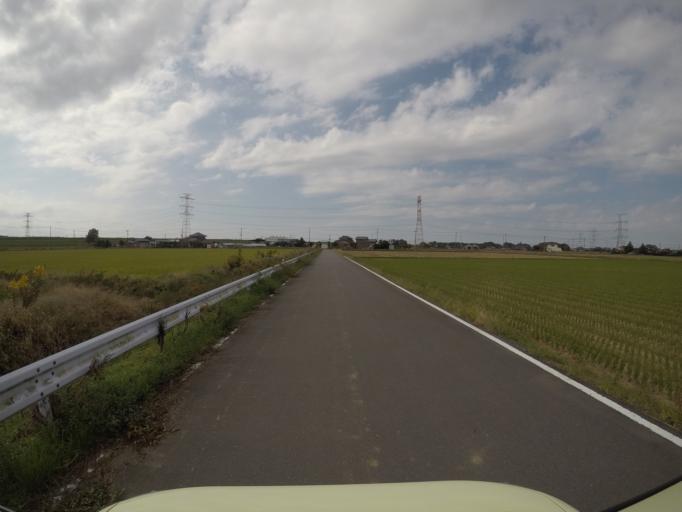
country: JP
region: Chiba
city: Noda
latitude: 35.9799
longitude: 139.9098
